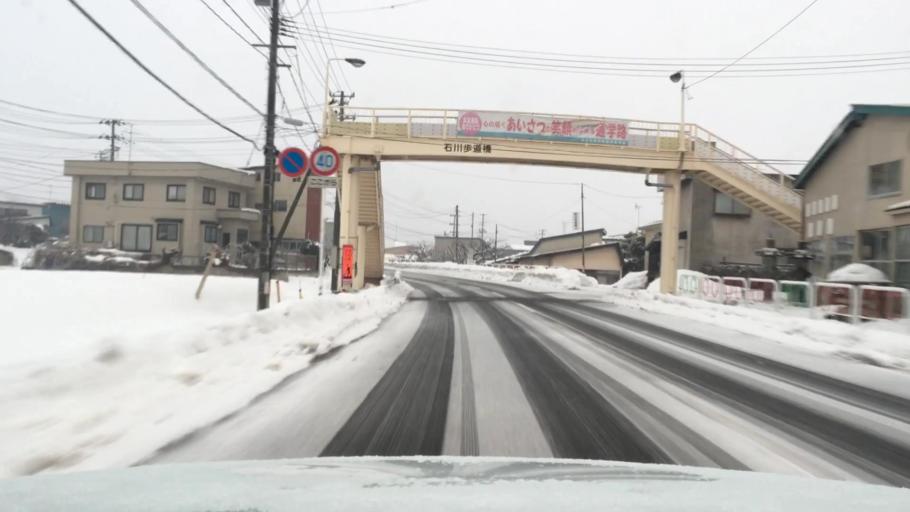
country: JP
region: Aomori
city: Hirosaki
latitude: 40.5504
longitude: 140.5489
